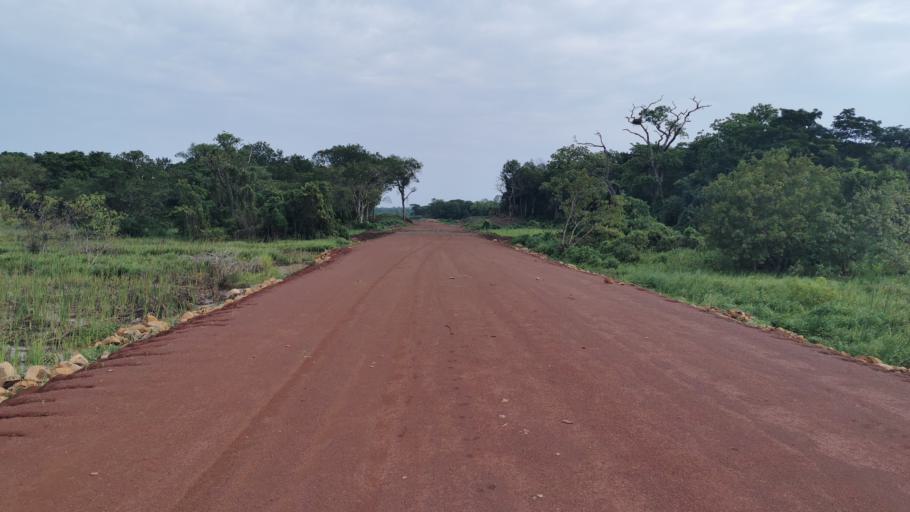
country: ET
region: Gambela
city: Gambela
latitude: 7.8708
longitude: 34.4952
